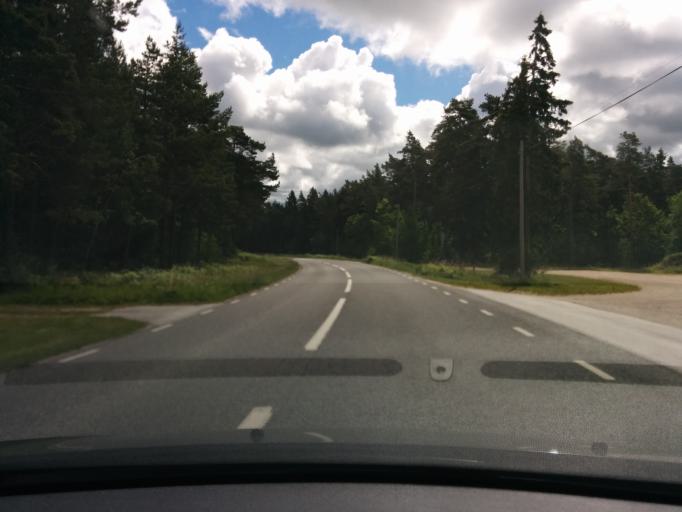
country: SE
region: Gotland
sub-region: Gotland
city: Visby
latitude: 57.6343
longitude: 18.5331
